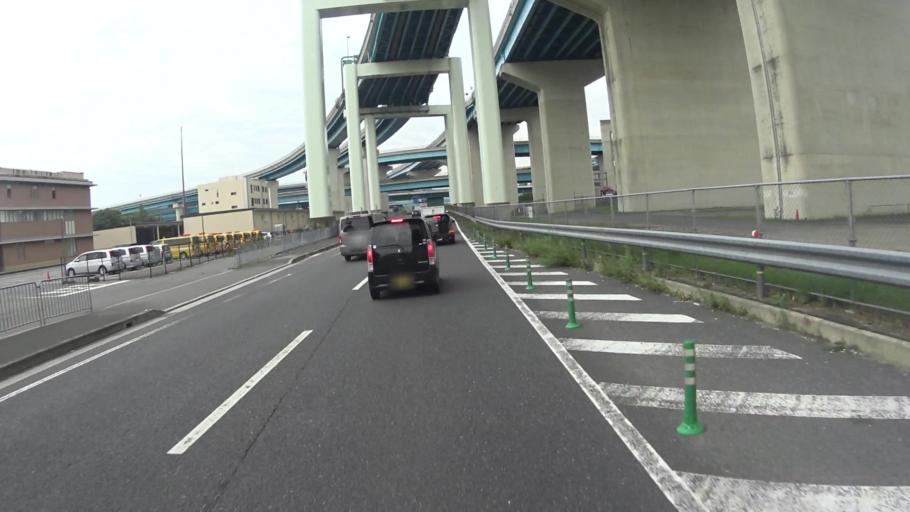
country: JP
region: Kyoto
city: Yawata
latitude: 34.8976
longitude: 135.7462
